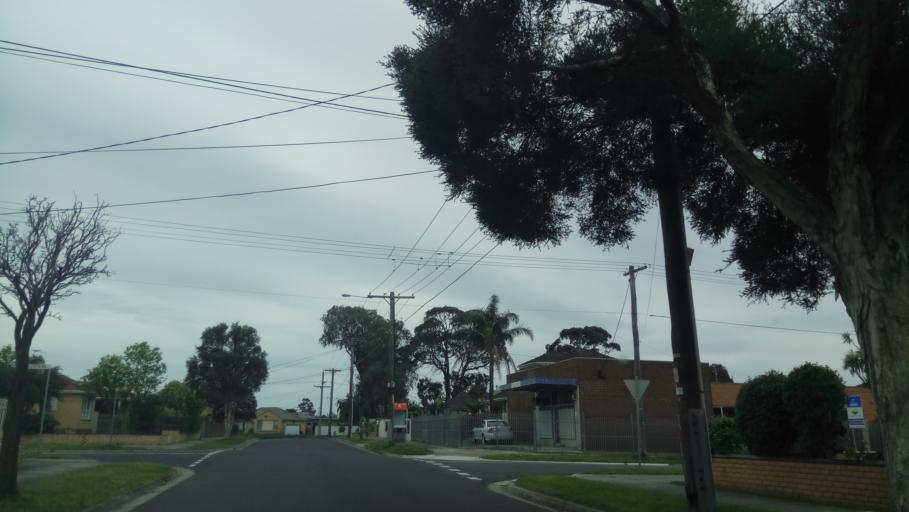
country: AU
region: Victoria
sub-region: Greater Dandenong
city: Springvale South
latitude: -37.9570
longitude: 145.1455
